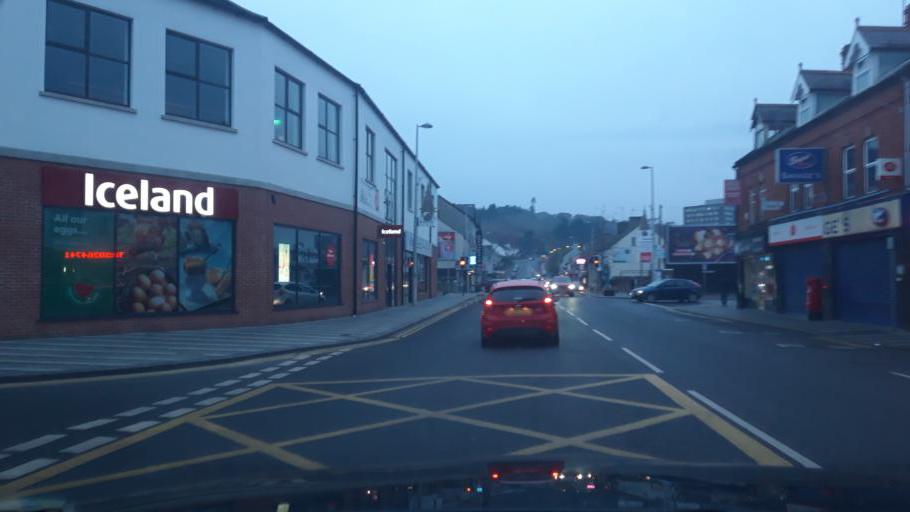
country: GB
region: Northern Ireland
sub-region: Newry and Mourne District
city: Newry
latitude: 54.1771
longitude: -6.3432
